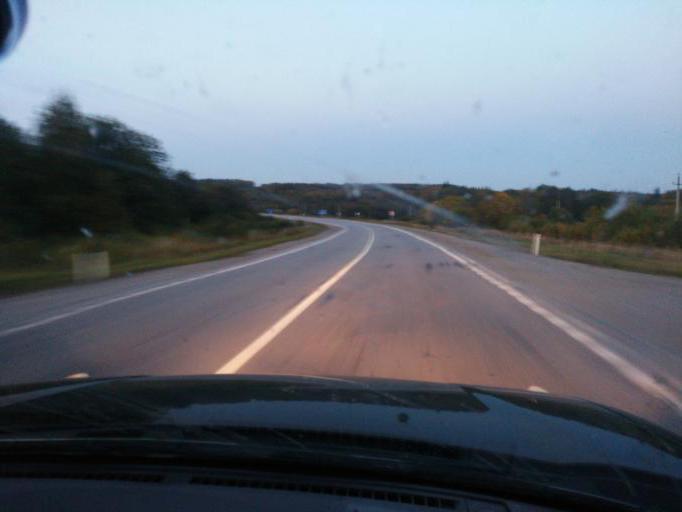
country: RU
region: Perm
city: Verkhnechusovskiye Gorodki
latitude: 58.2645
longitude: 57.3360
